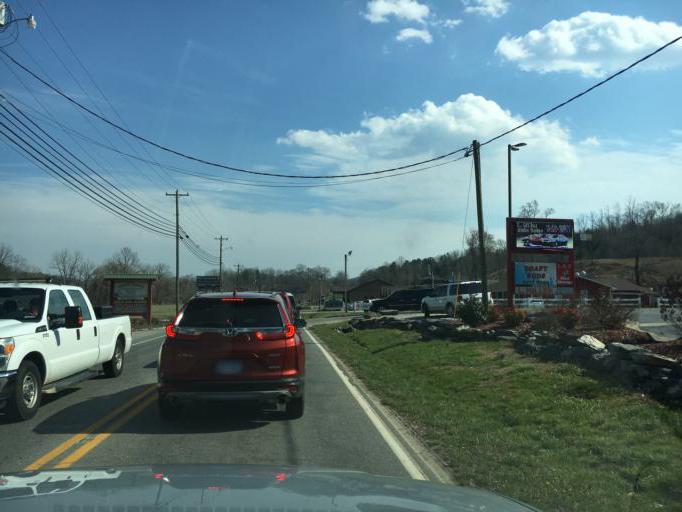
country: US
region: North Carolina
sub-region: McDowell County
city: Marion
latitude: 35.6679
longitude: -81.9821
